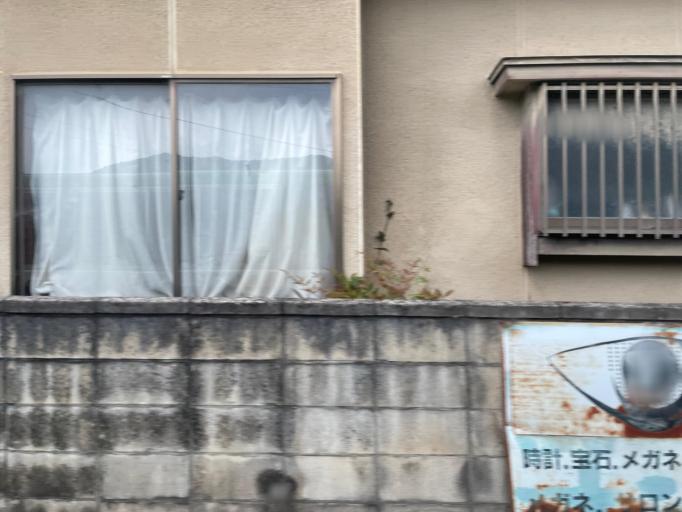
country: JP
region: Tochigi
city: Tanuma
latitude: 36.4615
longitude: 139.6360
